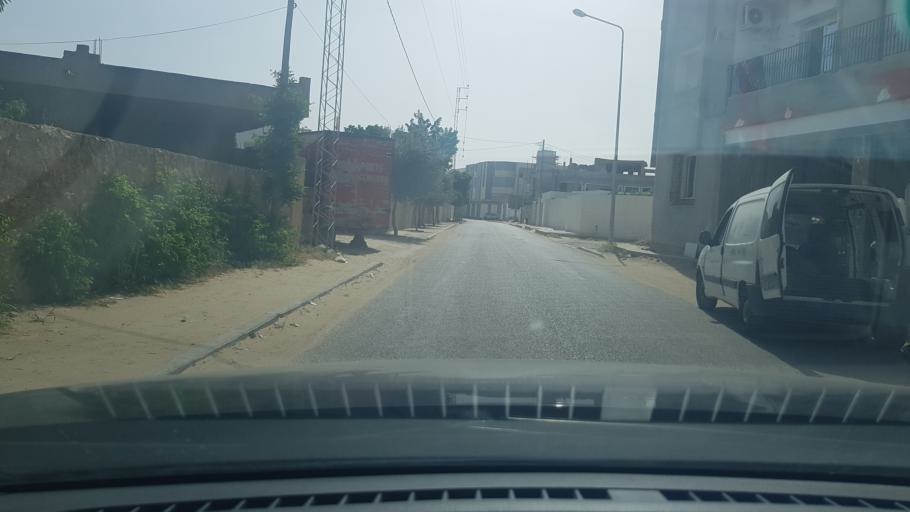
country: TN
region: Safaqis
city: Al Qarmadah
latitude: 34.8066
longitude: 10.7653
